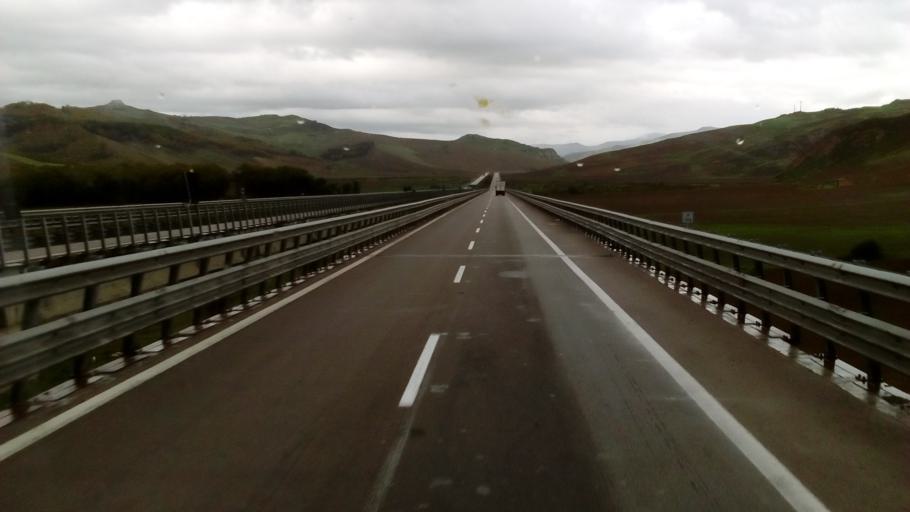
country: IT
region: Sicily
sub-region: Enna
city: Villarosa
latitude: 37.5509
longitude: 14.1423
